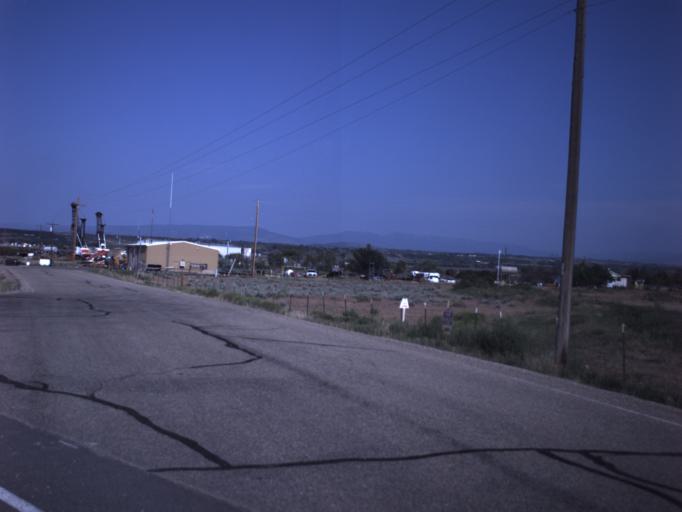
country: US
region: Utah
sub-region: Duchesne County
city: Duchesne
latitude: 40.3591
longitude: -110.3069
